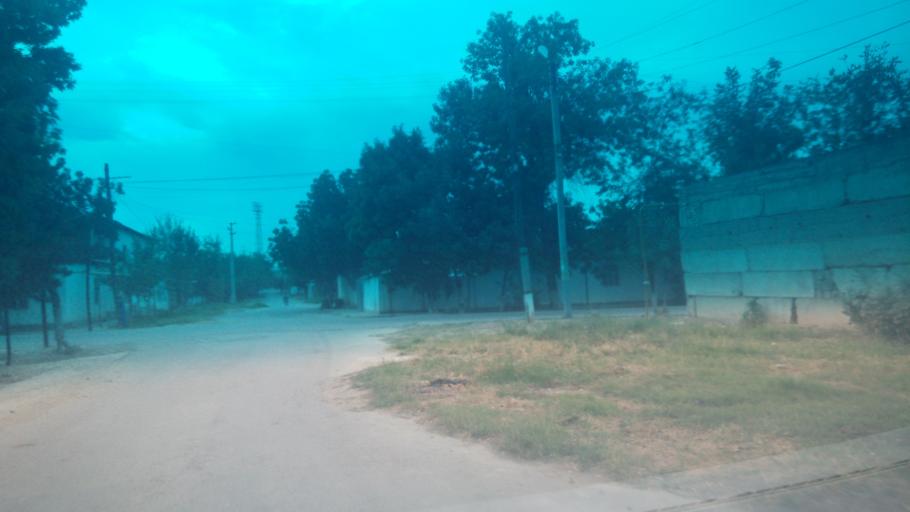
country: UZ
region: Sirdaryo
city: Guliston
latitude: 40.5024
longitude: 68.7795
